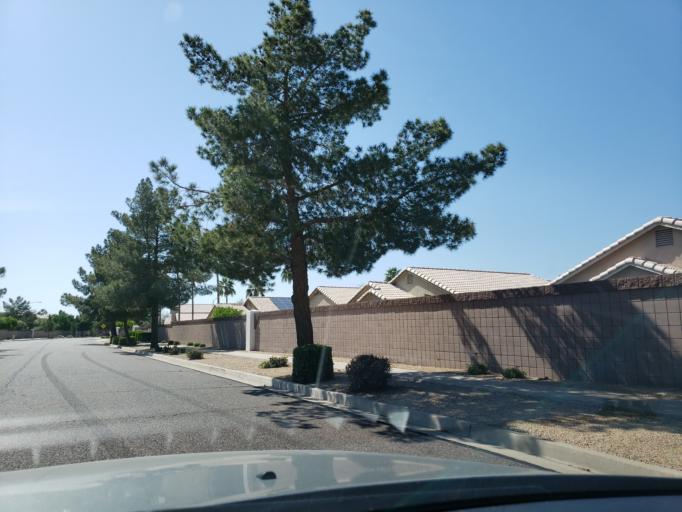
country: US
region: Arizona
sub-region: Maricopa County
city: Glendale
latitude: 33.5507
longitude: -112.1746
